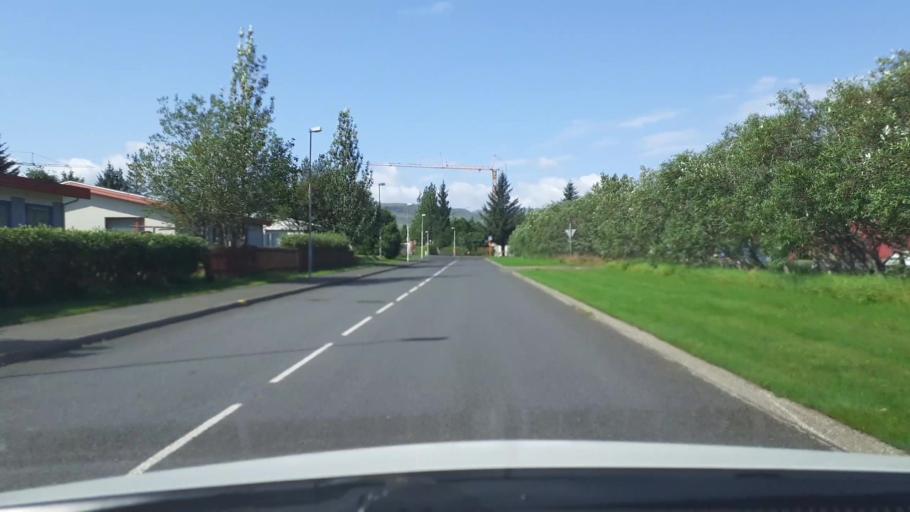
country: IS
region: South
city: Hveragerdi
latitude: 63.9949
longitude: -21.1779
